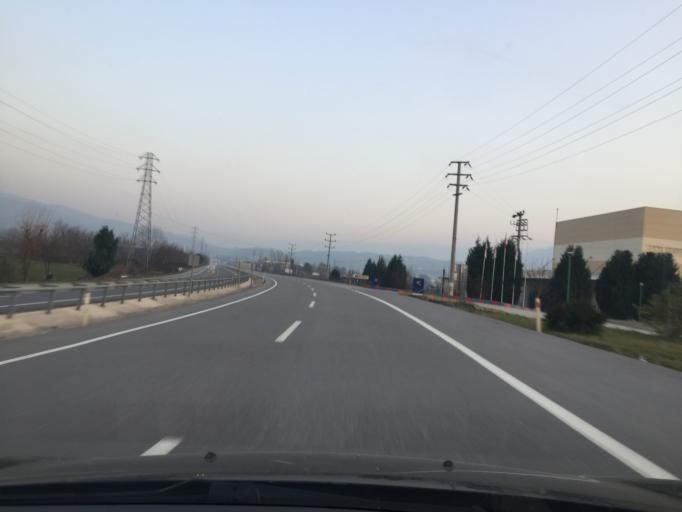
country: TR
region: Sakarya
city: Akyazi
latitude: 40.6405
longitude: 30.6148
